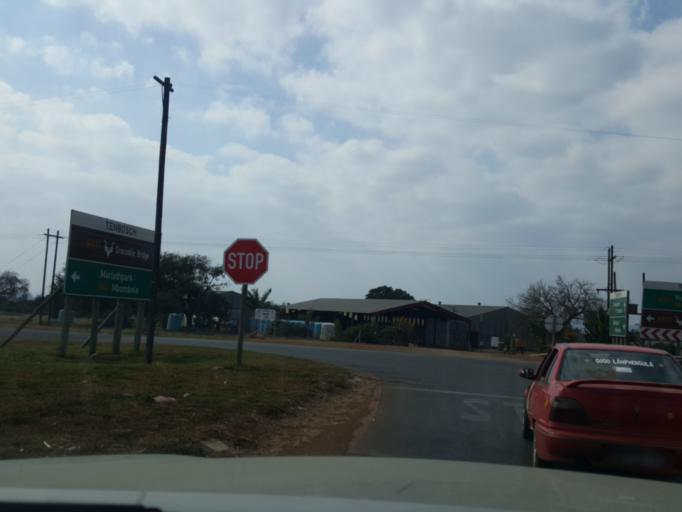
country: ZA
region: Mpumalanga
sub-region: Ehlanzeni District
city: Komatipoort
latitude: -25.3915
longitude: 31.9140
